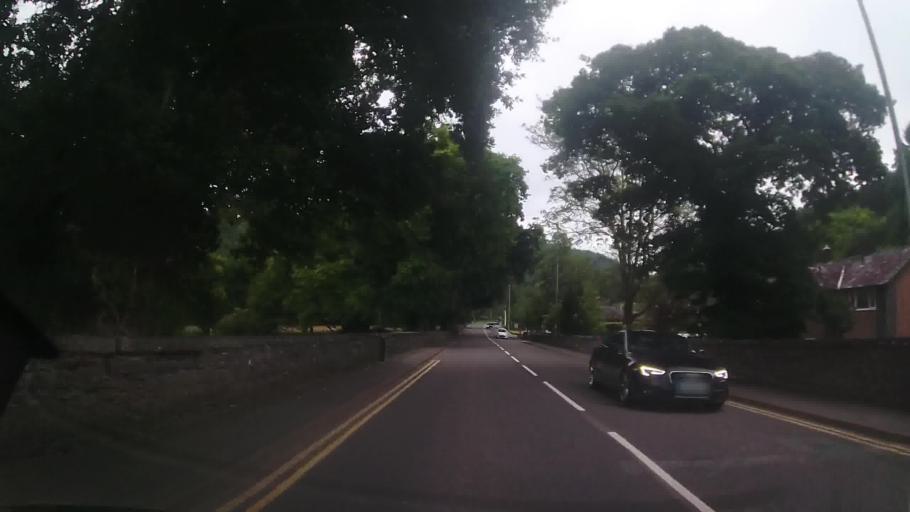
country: GB
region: Wales
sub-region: Conwy
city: Betws-y-Coed
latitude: 53.0882
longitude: -3.7993
